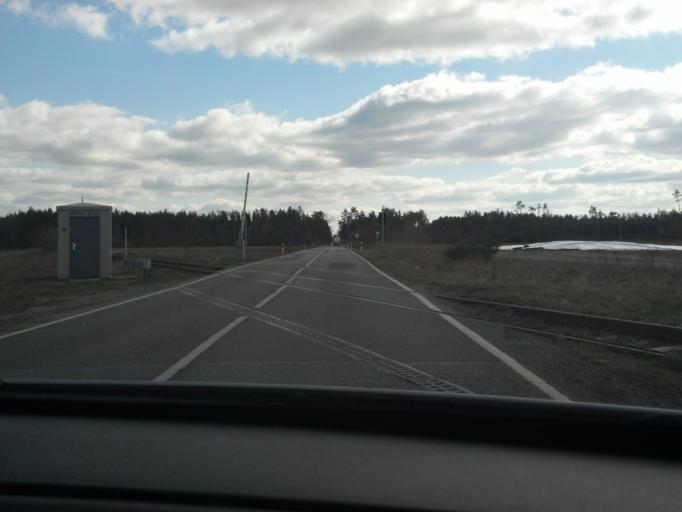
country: DE
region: Mecklenburg-Vorpommern
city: Plau am See
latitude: 53.3735
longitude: 12.2473
